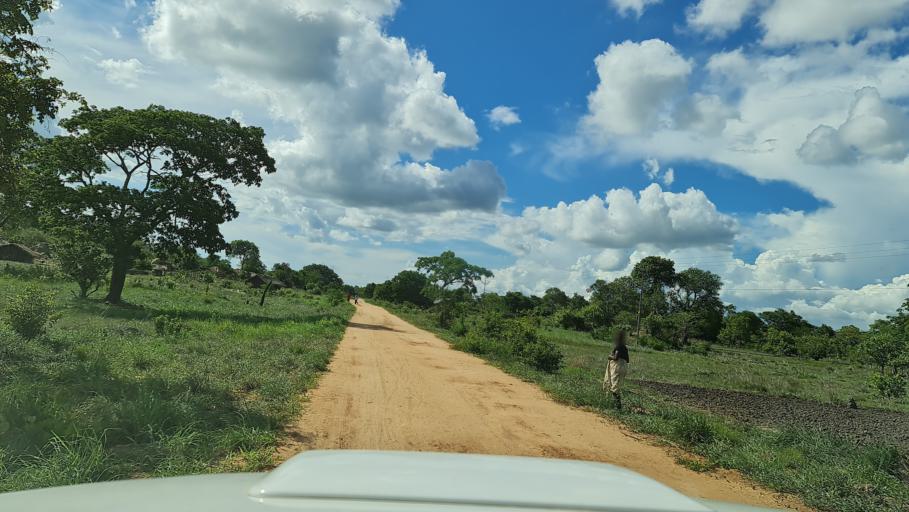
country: MZ
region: Nampula
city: Ilha de Mocambique
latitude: -15.4067
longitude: 40.2429
